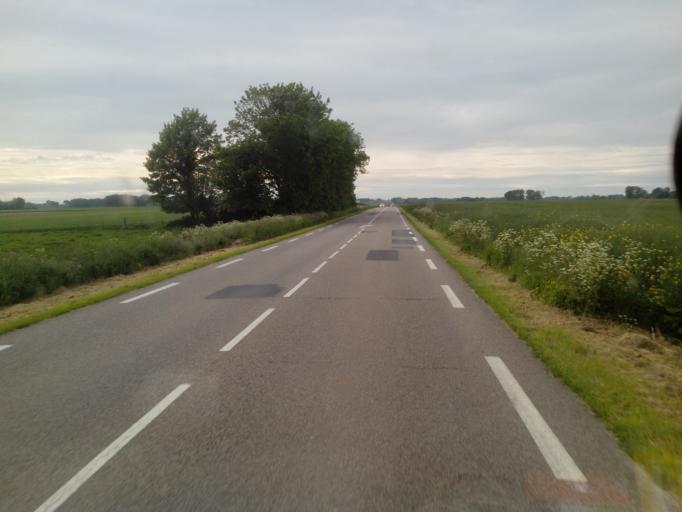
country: FR
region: Haute-Normandie
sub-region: Departement de la Seine-Maritime
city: Fauville-en-Caux
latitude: 49.6625
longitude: 0.5874
